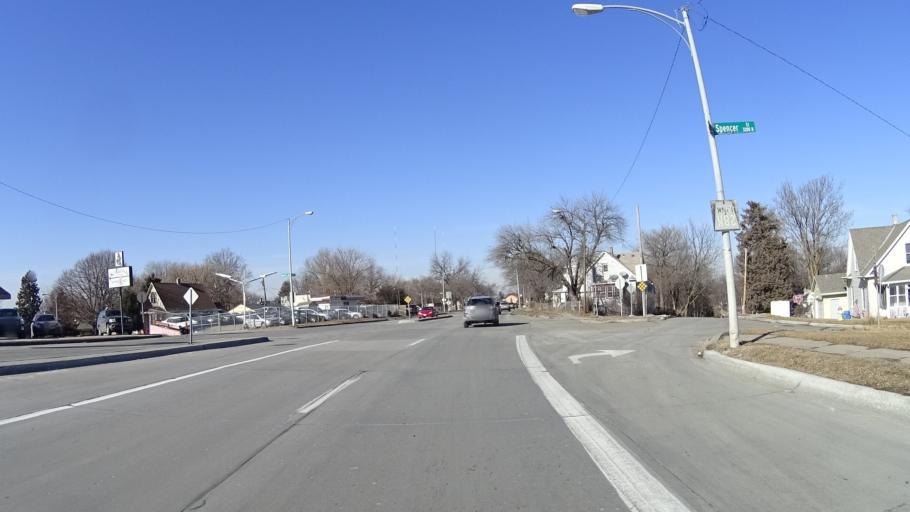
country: US
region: Nebraska
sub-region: Douglas County
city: Omaha
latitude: 41.2875
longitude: -96.0095
